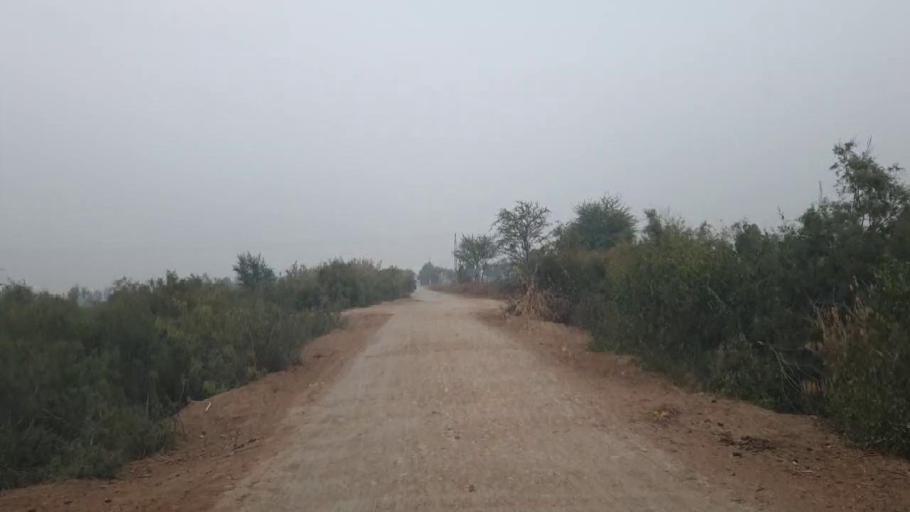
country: PK
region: Sindh
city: Tando Adam
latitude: 25.7544
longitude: 68.7025
